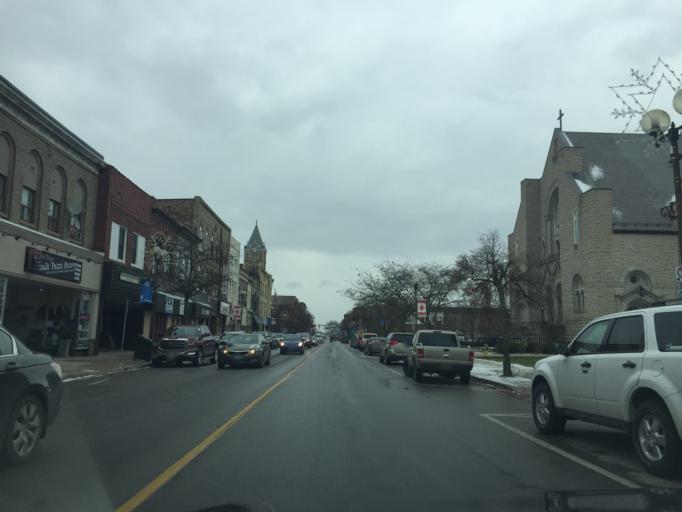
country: CA
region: Ontario
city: St. Thomas
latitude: 42.7789
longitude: -81.1946
